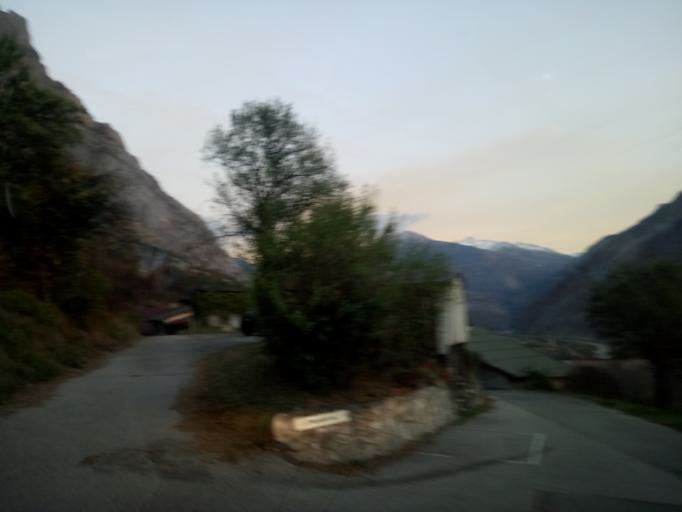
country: FR
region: Rhone-Alpes
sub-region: Departement de la Savoie
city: Saint-Michel-de-Maurienne
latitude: 45.2529
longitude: 6.4254
